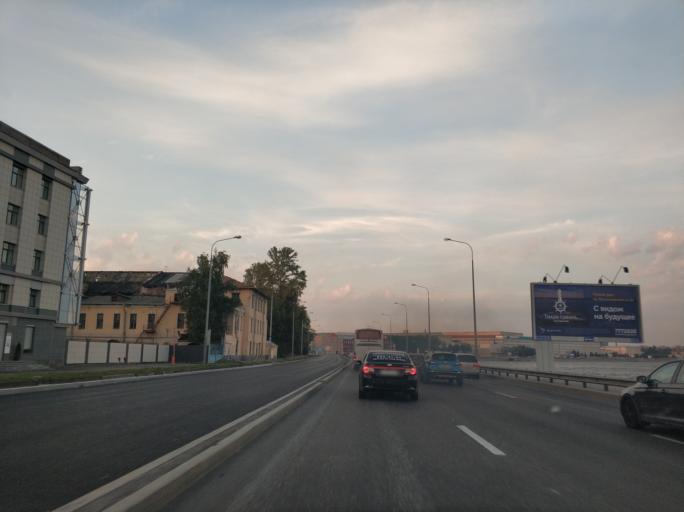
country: RU
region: Leningrad
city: Finlyandskiy
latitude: 59.9560
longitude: 30.3770
